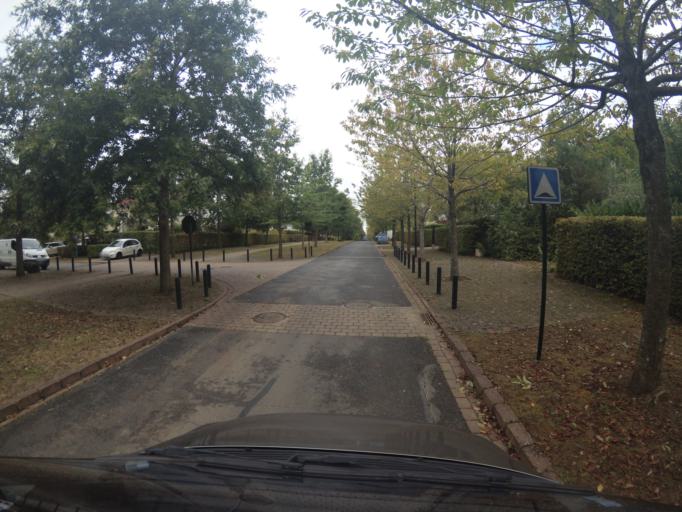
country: FR
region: Ile-de-France
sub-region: Departement de Seine-et-Marne
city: Montevrain
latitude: 48.8760
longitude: 2.7569
